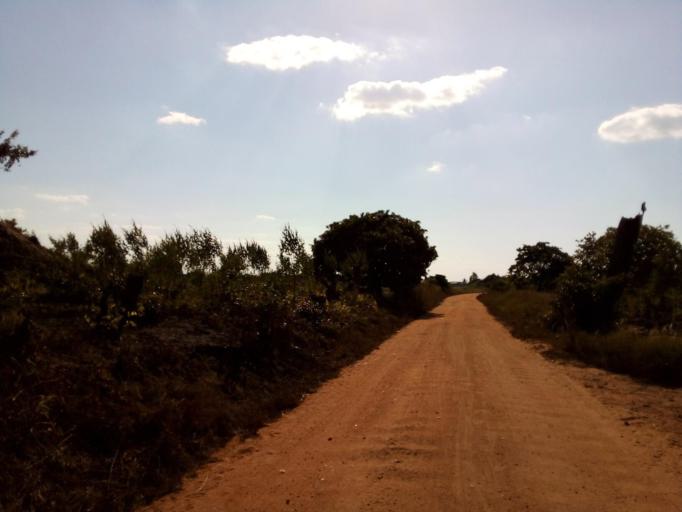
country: MZ
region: Zambezia
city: Quelimane
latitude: -17.5694
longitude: 36.6387
